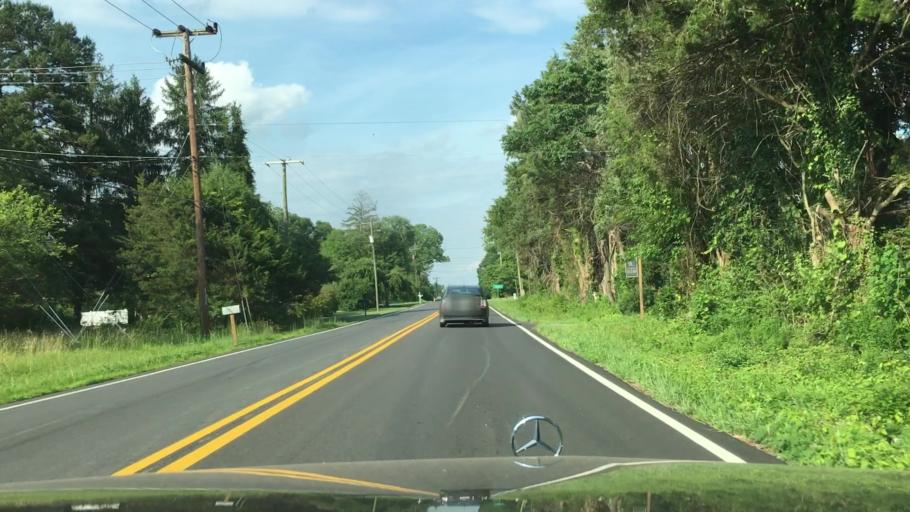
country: US
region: Virginia
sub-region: Orange County
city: Gordonsville
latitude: 38.1367
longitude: -78.1984
